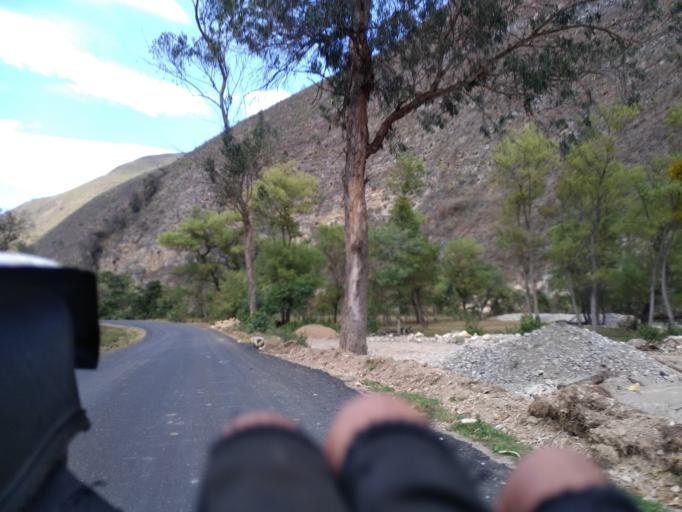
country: PE
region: Amazonas
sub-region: Provincia de Chachapoyas
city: Duraznopampa
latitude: -6.5743
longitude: -77.8272
